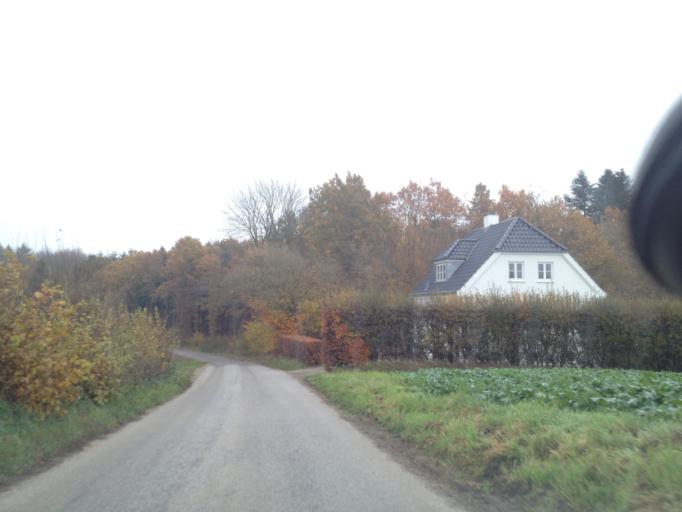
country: DK
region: South Denmark
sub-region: Assens Kommune
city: Vissenbjerg
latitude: 55.4240
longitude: 10.1890
